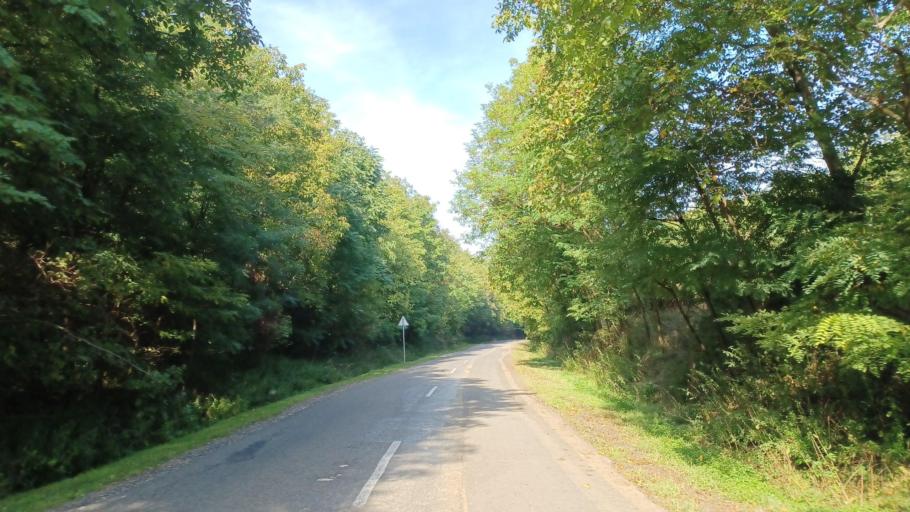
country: HU
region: Tolna
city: Pincehely
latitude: 46.6766
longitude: 18.4672
